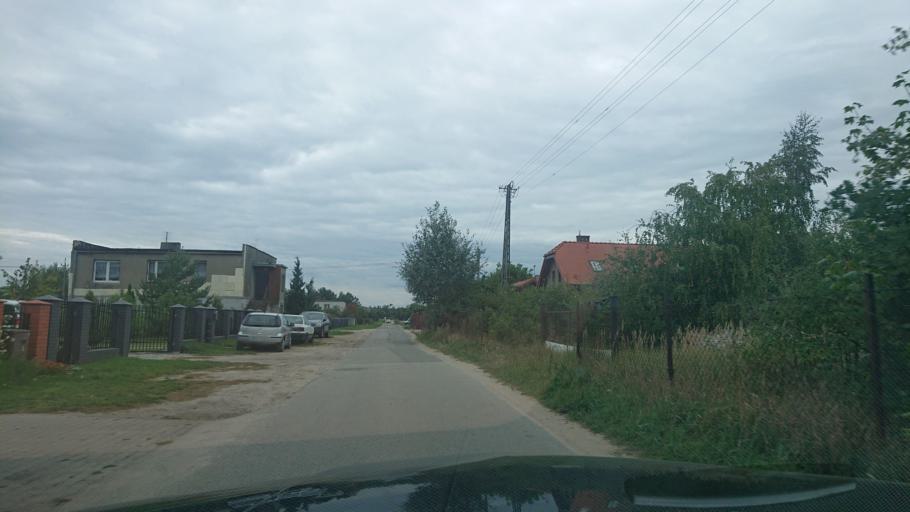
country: PL
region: Greater Poland Voivodeship
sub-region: Powiat gnieznienski
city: Gniezno
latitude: 52.4824
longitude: 17.6030
